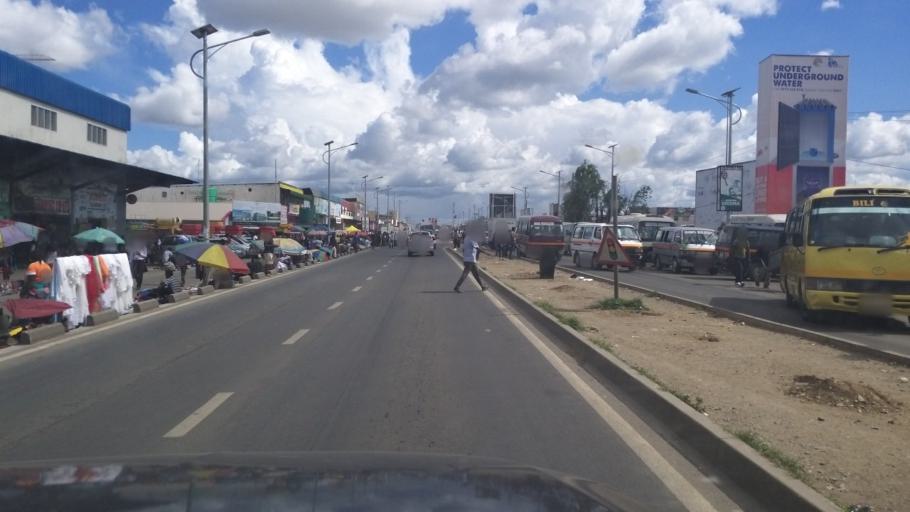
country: ZM
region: Lusaka
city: Lusaka
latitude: -15.4189
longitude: 28.2779
